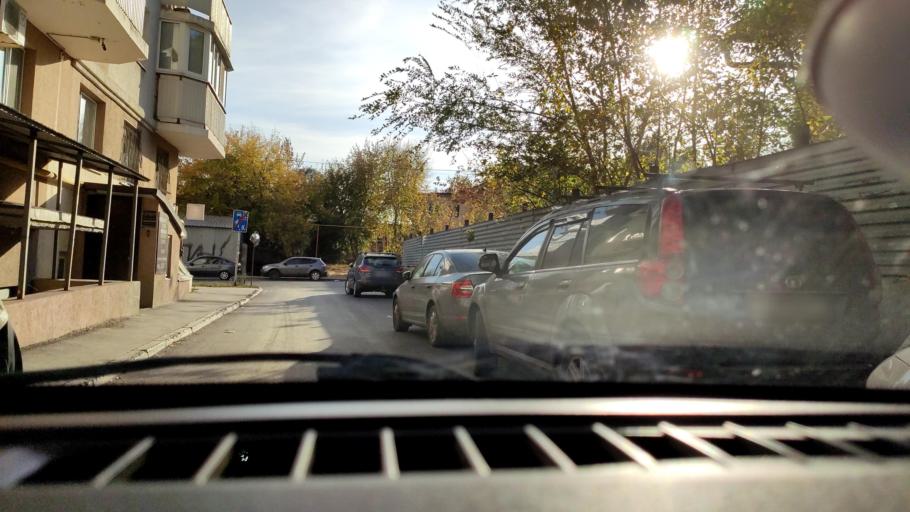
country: RU
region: Samara
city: Samara
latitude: 53.1817
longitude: 50.0934
